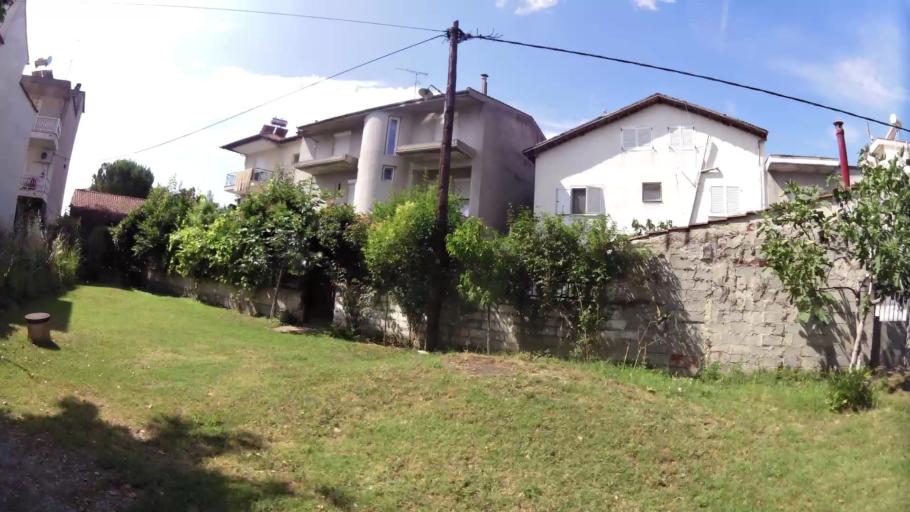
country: GR
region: Central Macedonia
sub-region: Nomos Pierias
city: Katerini
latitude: 40.2737
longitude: 22.4879
